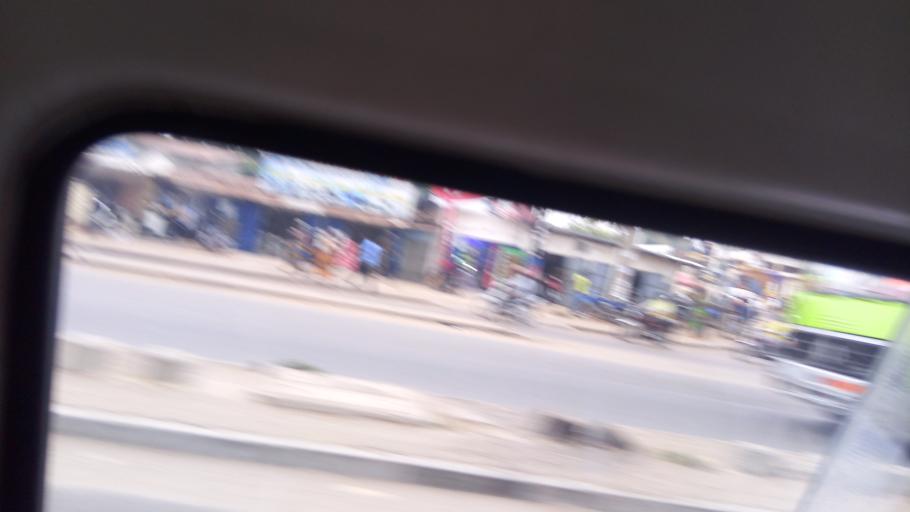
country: BJ
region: Atlantique
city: Abomey-Calavi
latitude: 6.4054
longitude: 2.3415
